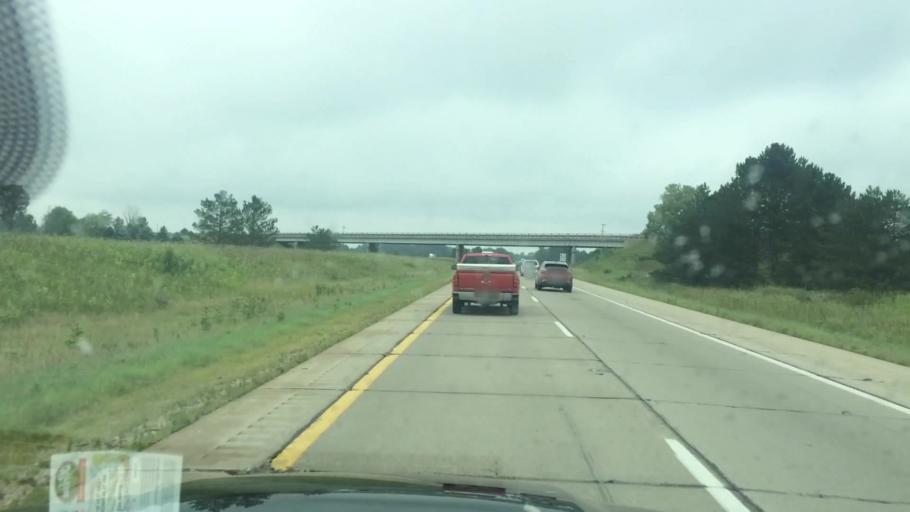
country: US
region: Michigan
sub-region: Eaton County
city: Charlotte
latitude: 42.5142
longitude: -84.8379
